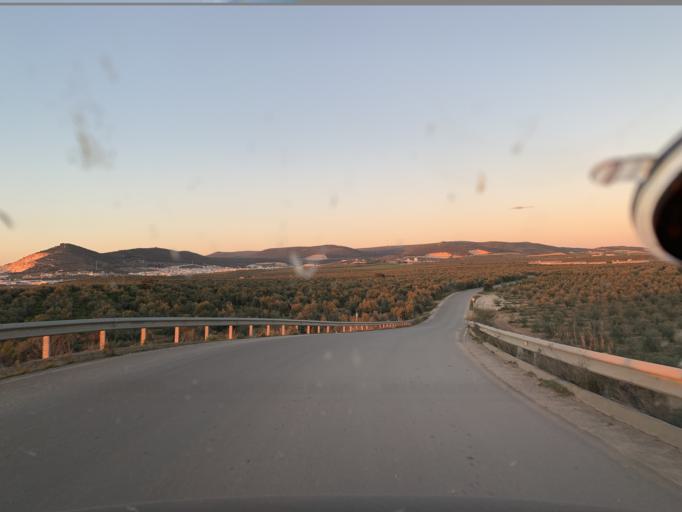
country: ES
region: Andalusia
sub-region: Provincia de Sevilla
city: Gilena
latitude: 37.2261
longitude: -4.9331
